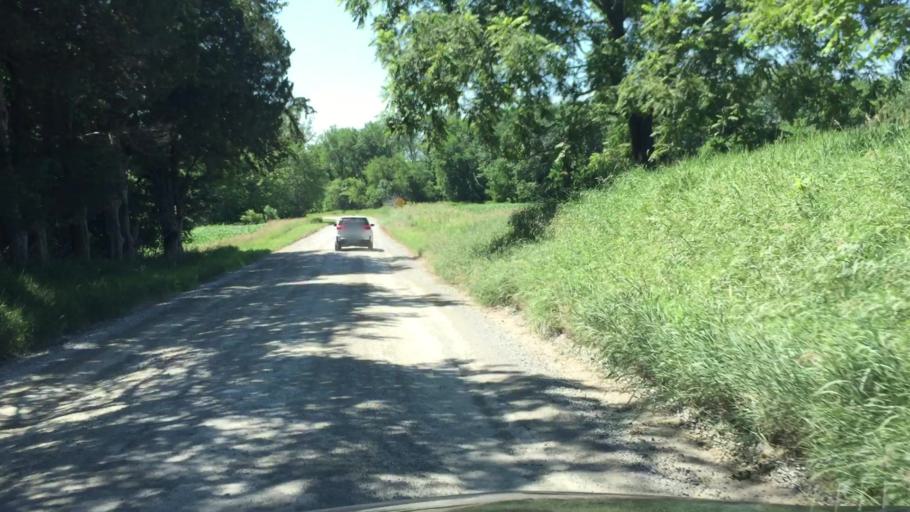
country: US
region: Iowa
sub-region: Linn County
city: Ely
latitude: 41.8203
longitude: -91.5895
